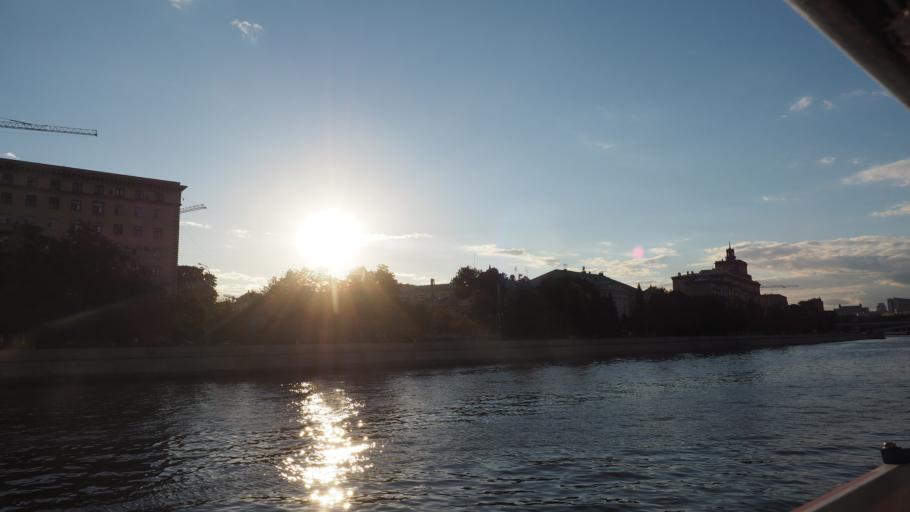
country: RU
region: Moscow
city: Zamoskvorech'ye
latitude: 55.7410
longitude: 37.6454
